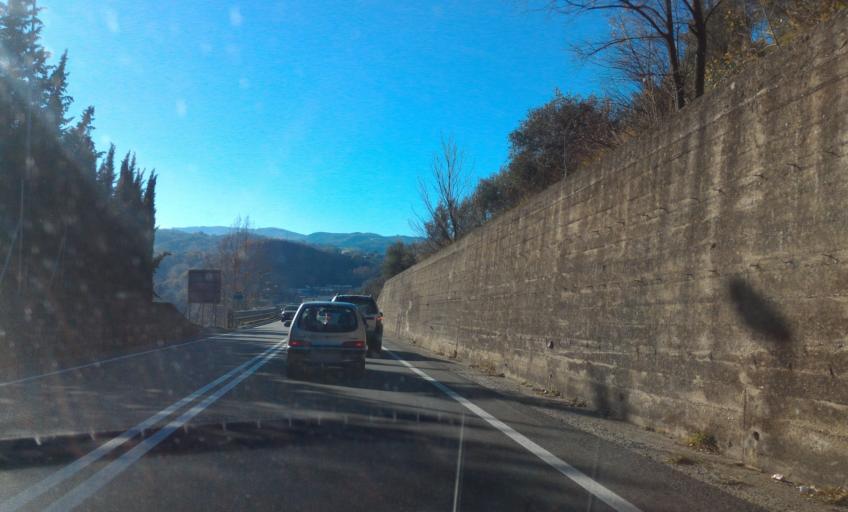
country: IT
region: Calabria
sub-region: Provincia di Cosenza
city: Cosenza
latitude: 39.2953
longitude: 16.2659
